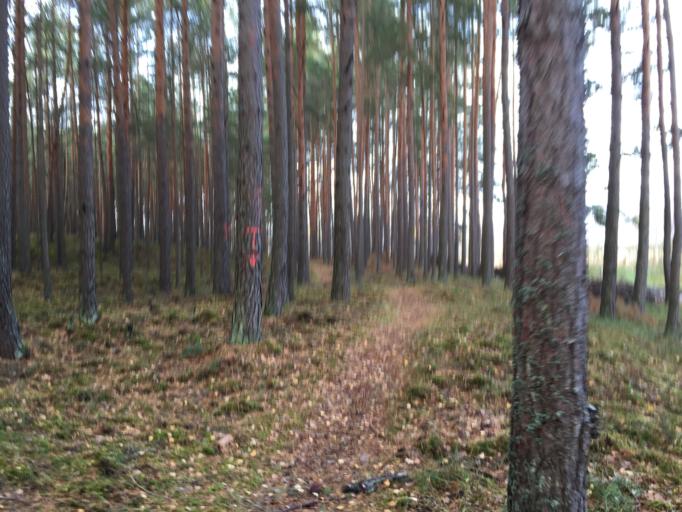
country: LV
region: Carnikava
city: Carnikava
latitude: 57.1479
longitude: 24.2634
